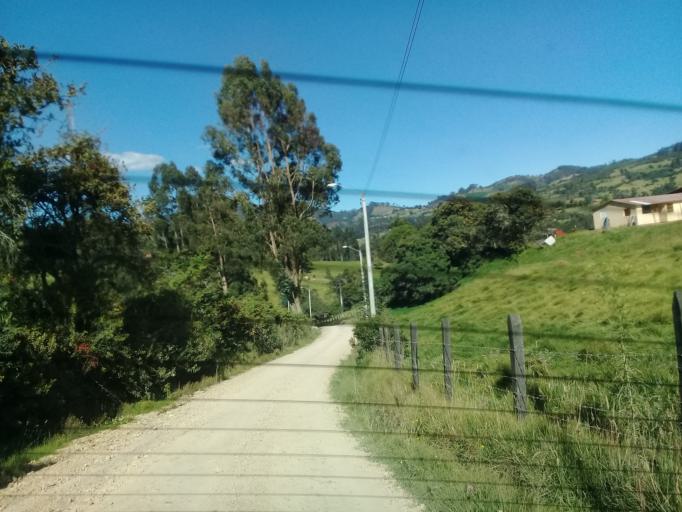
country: CO
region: Cundinamarca
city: Zipaquira
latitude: 5.0041
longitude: -74.0709
